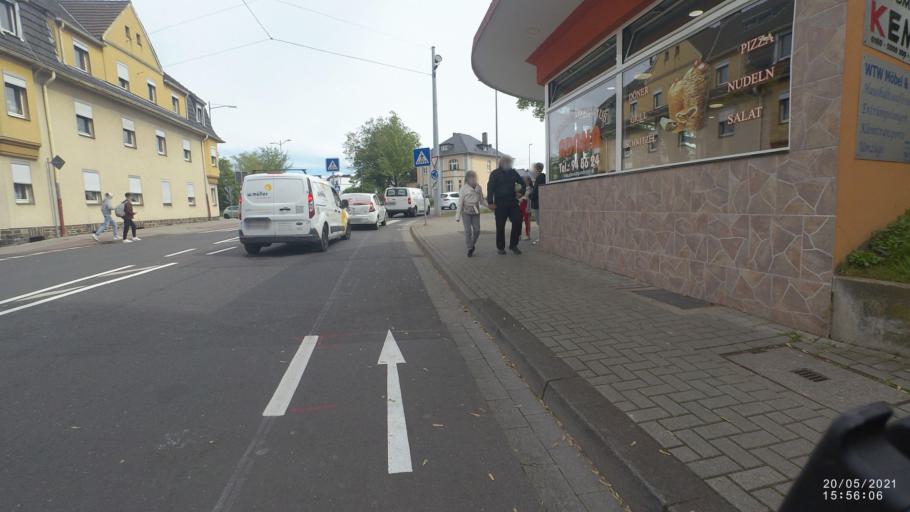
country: DE
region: Rheinland-Pfalz
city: Andernach
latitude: 50.4323
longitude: 7.4078
